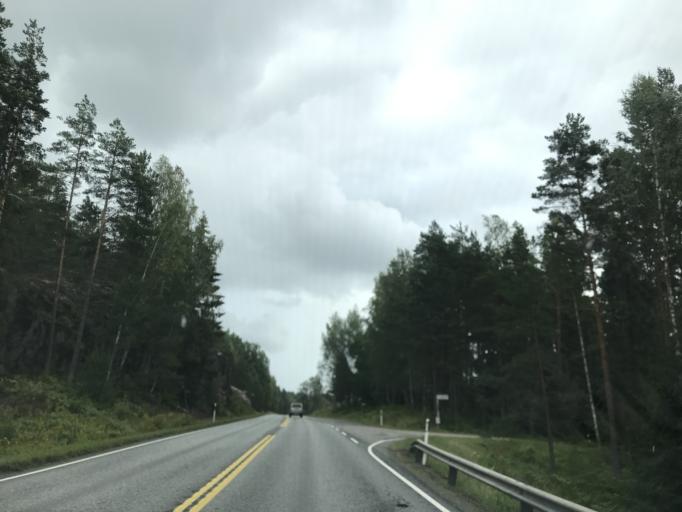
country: FI
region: Varsinais-Suomi
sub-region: Salo
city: Pernioe
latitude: 60.0811
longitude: 23.2411
